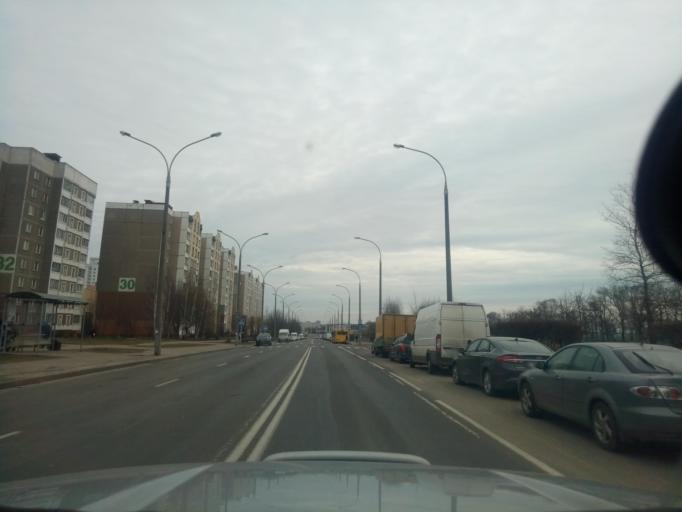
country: BY
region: Minsk
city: Syenitsa
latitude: 53.8345
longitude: 27.5818
